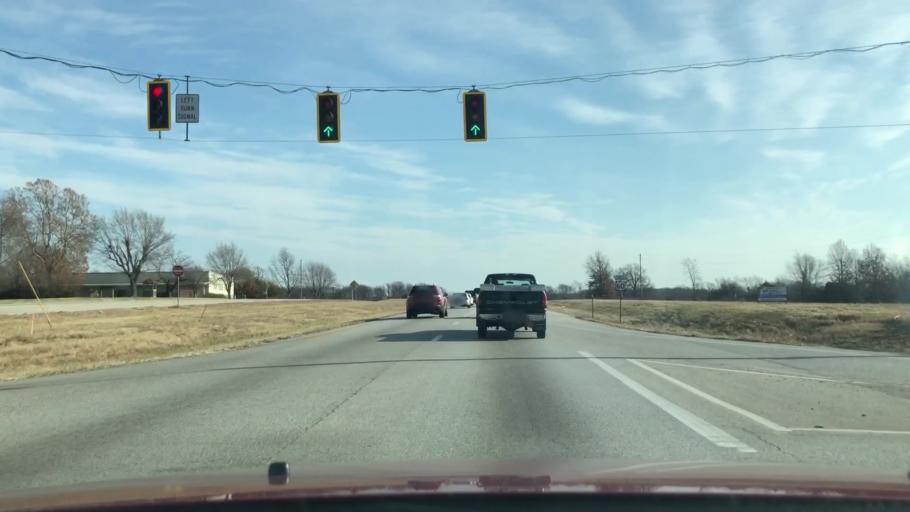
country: US
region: Missouri
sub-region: Webster County
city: Rogersville
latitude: 37.1187
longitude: -93.1193
